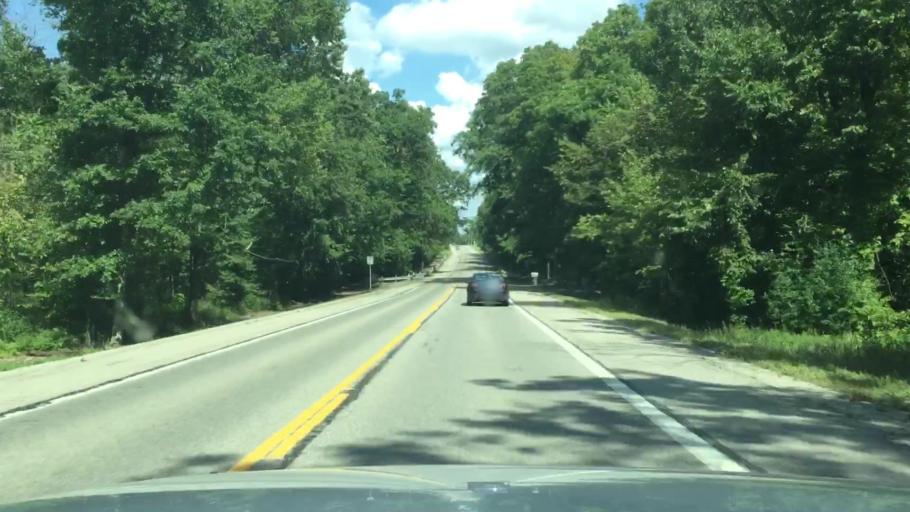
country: US
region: Michigan
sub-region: Lenawee County
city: Clinton
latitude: 42.1128
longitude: -83.8849
